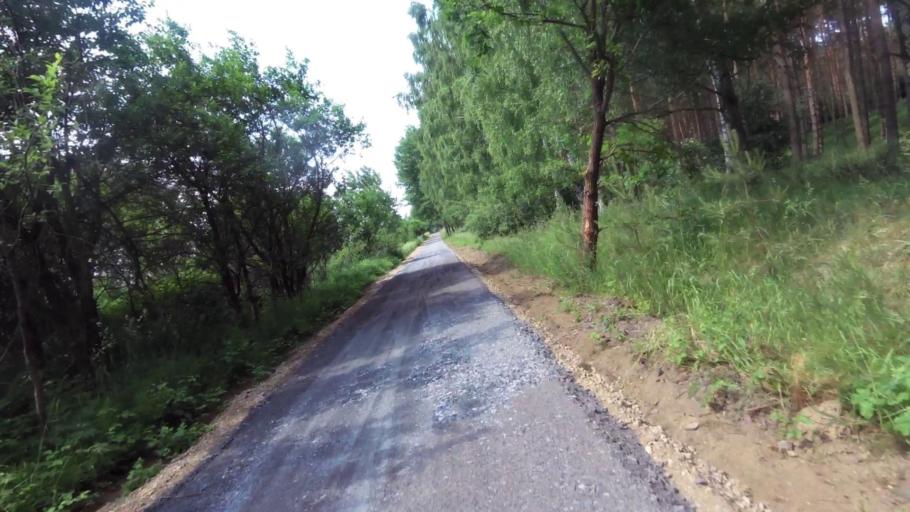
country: PL
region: West Pomeranian Voivodeship
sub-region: Powiat pyrzycki
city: Bielice
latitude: 53.2045
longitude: 14.6167
